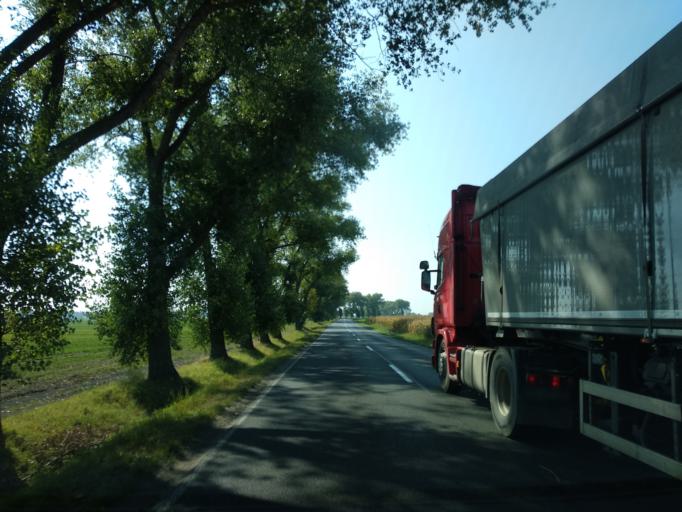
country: PL
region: Lower Silesian Voivodeship
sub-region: Powiat strzelinski
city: Strzelin
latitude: 50.8229
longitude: 17.0606
